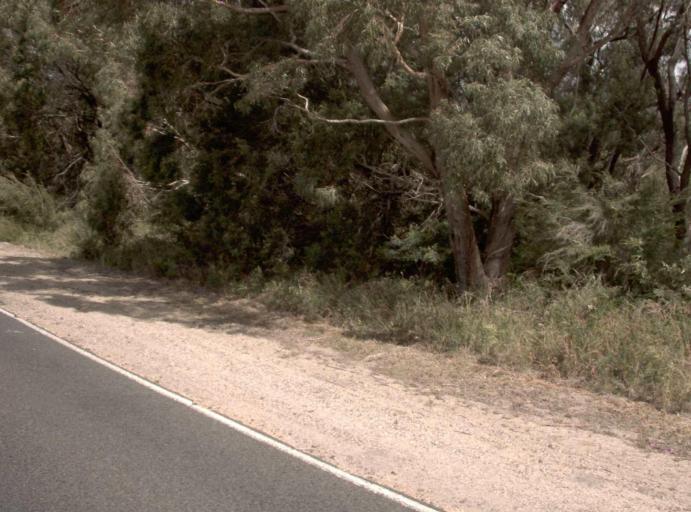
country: AU
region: Victoria
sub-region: Wellington
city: Sale
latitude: -38.1621
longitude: 146.8806
